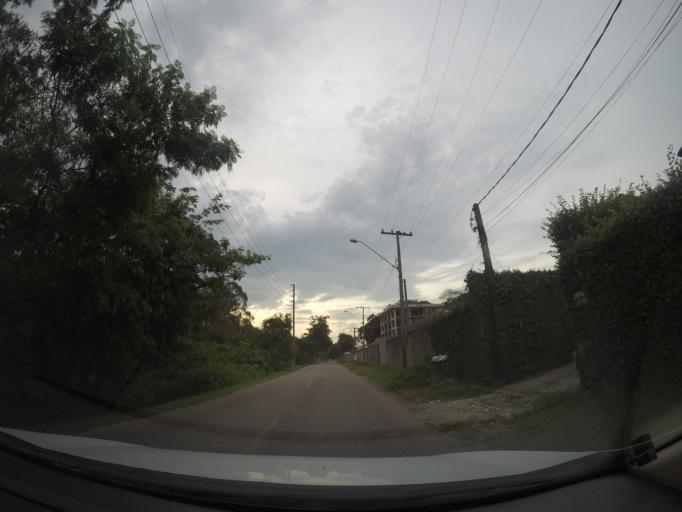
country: BR
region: Parana
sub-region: Curitiba
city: Curitiba
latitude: -25.4682
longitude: -49.2482
